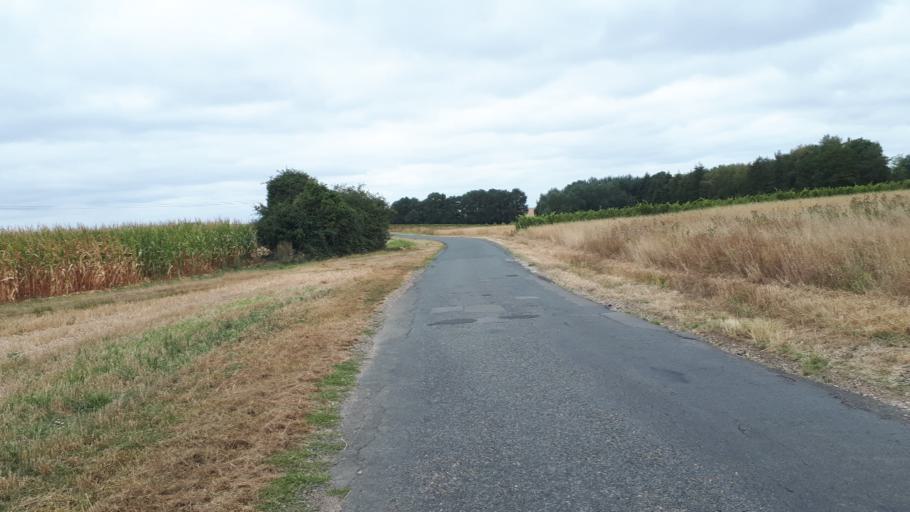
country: FR
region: Centre
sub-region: Departement du Loir-et-Cher
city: Villiers-sur-Loir
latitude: 47.8228
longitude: 0.9982
